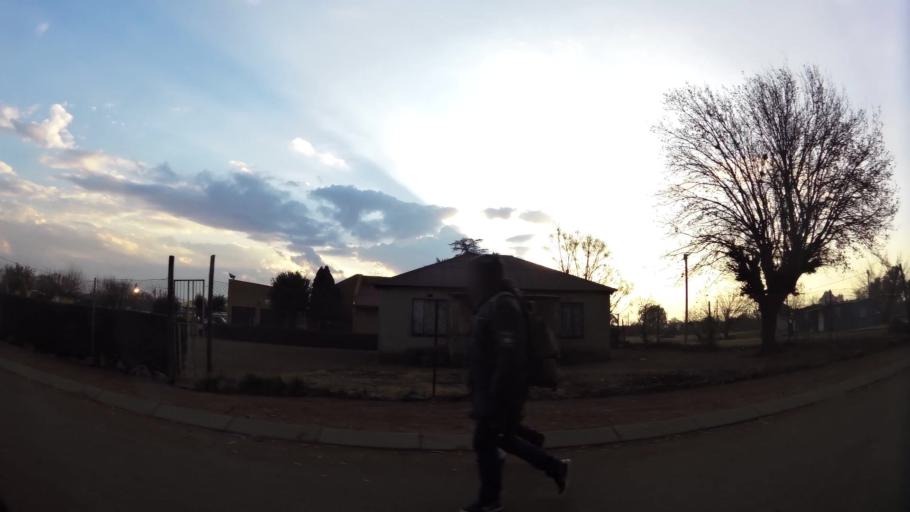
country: ZA
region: Gauteng
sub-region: City of Johannesburg Metropolitan Municipality
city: Orange Farm
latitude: -26.5394
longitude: 27.8495
